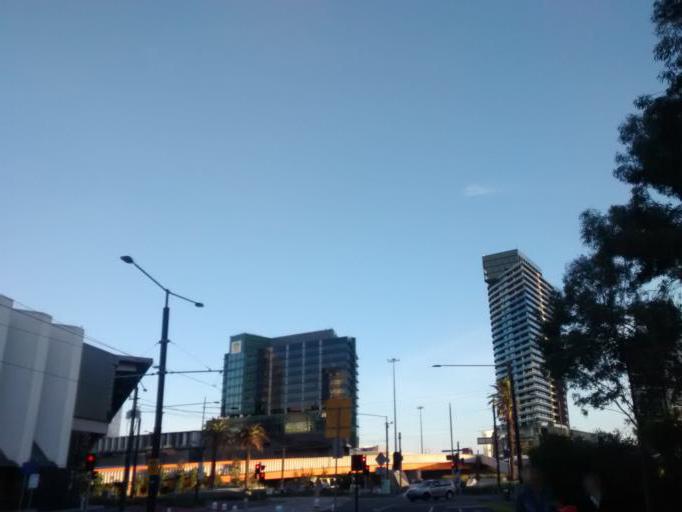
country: AU
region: Victoria
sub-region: Melbourne
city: Docklands
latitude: -37.8218
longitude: 144.9475
